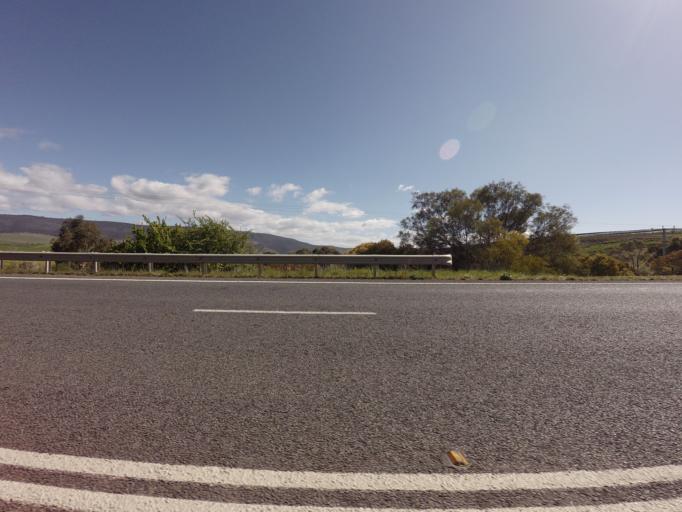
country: AU
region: Tasmania
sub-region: Derwent Valley
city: New Norfolk
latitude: -42.7155
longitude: 146.9466
